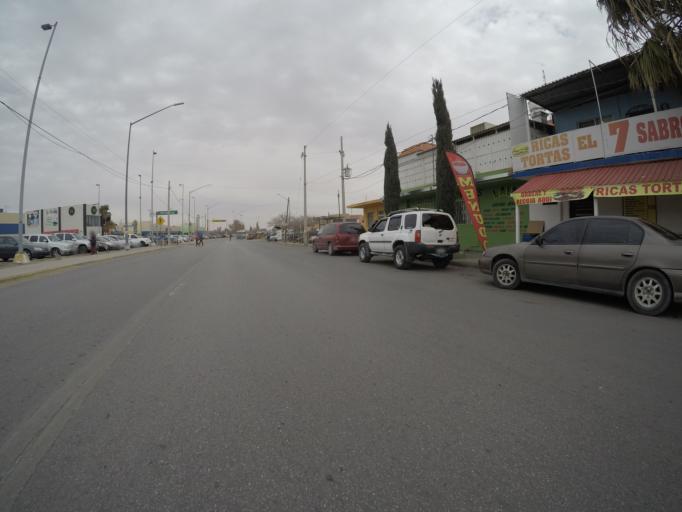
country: MX
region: Chihuahua
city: Ciudad Juarez
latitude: 31.7395
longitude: -106.4518
